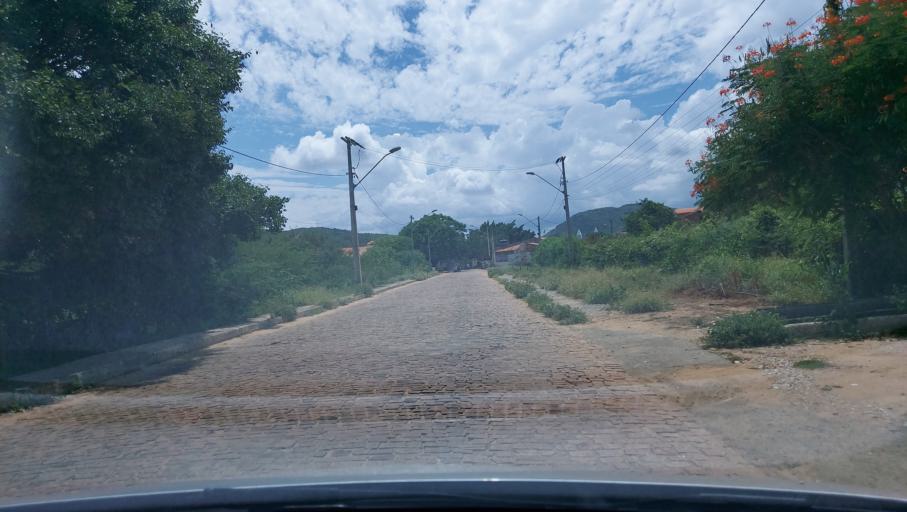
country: BR
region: Bahia
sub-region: Oliveira Dos Brejinhos
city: Beira Rio
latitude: -11.9954
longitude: -42.6295
